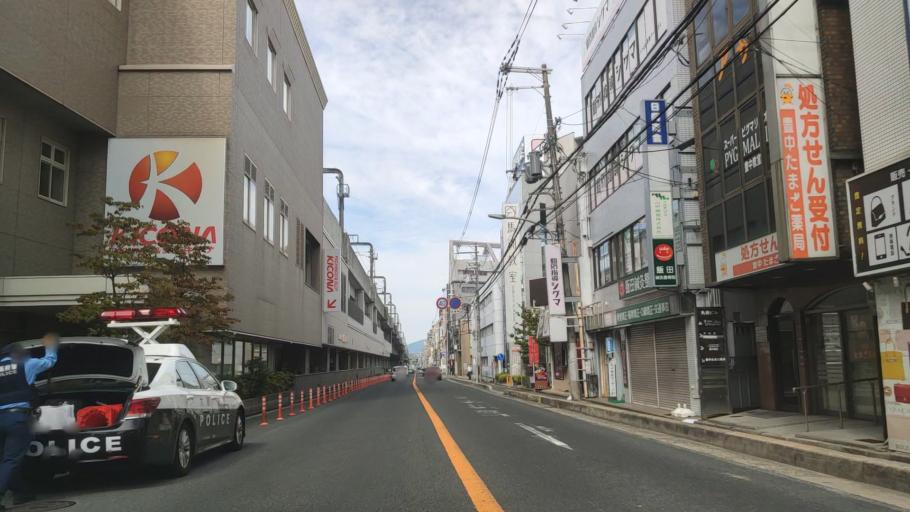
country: JP
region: Osaka
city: Toyonaka
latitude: 34.7880
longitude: 135.4609
